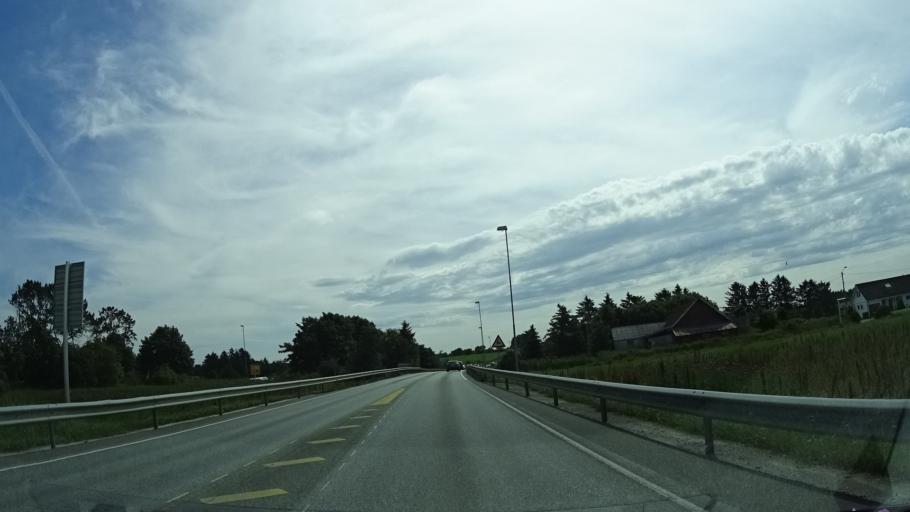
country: NO
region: Rogaland
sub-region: Randaberg
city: Randaberg
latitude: 59.0073
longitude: 5.6407
